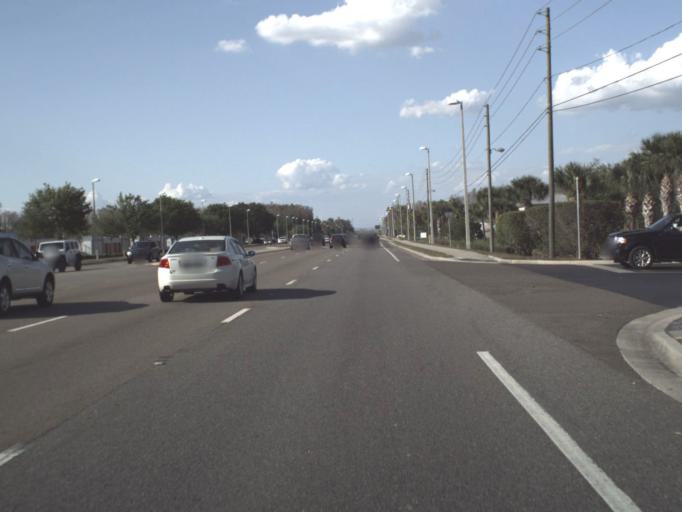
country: US
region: Florida
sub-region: Orange County
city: Hunters Creek
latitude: 28.3535
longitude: -81.4043
